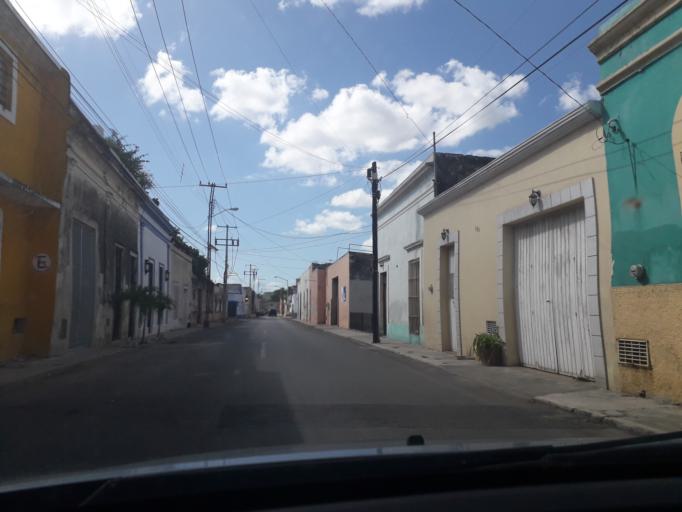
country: MX
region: Yucatan
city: Merida
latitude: 20.9600
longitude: -89.6264
